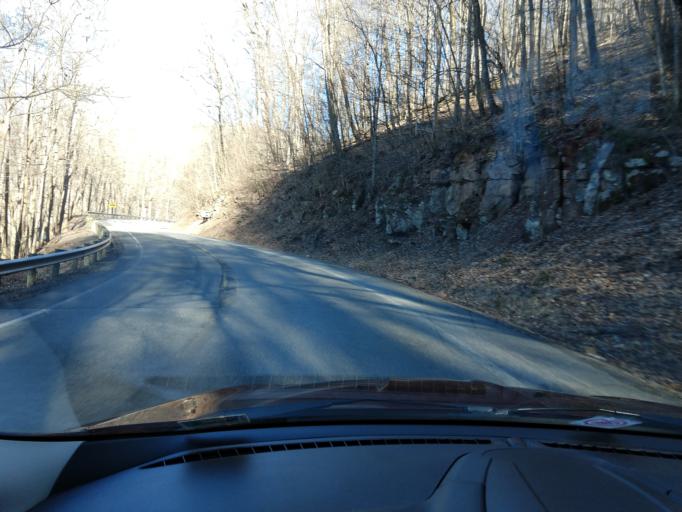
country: US
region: West Virginia
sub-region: Summers County
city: Hinton
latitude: 37.7517
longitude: -80.9018
